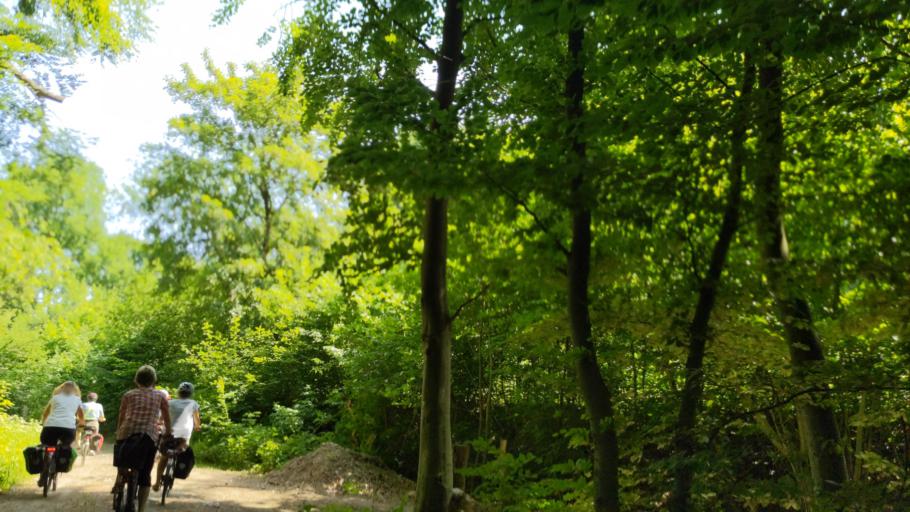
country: DE
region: Schleswig-Holstein
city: Fredeburg
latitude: 53.6718
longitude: 10.7192
